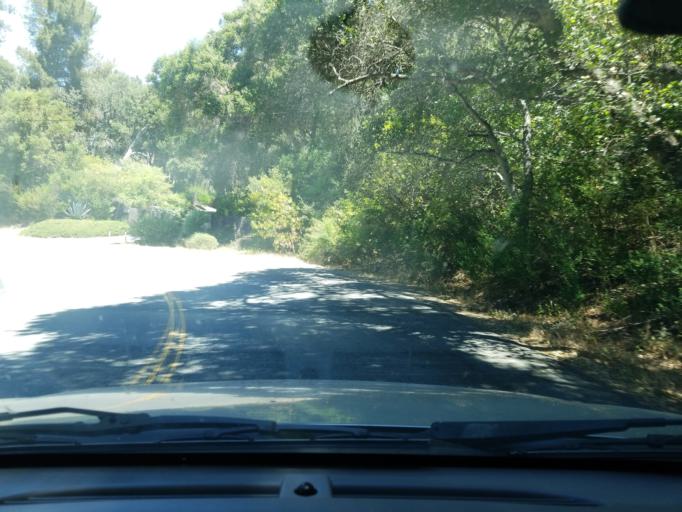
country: US
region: California
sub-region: Monterey County
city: Carmel Valley Village
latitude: 36.4581
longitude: -121.7062
